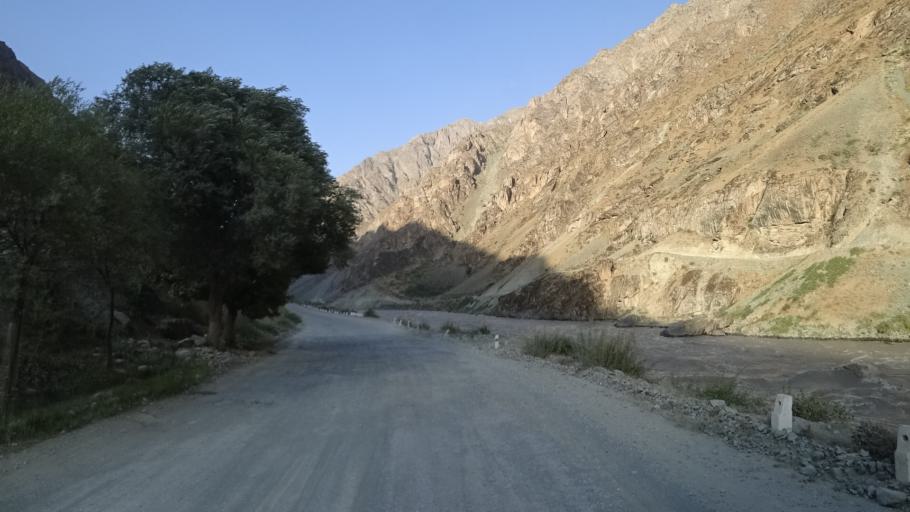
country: TJ
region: Gorno-Badakhshan
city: Qalaikhumb
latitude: 38.4173
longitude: 70.7352
